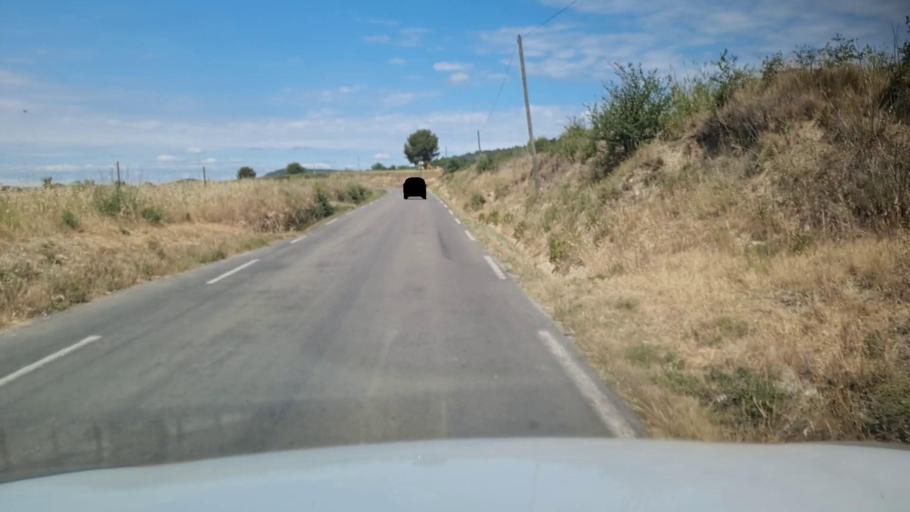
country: FR
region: Languedoc-Roussillon
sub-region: Departement du Gard
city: Caveirac
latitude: 43.8300
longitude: 4.2457
